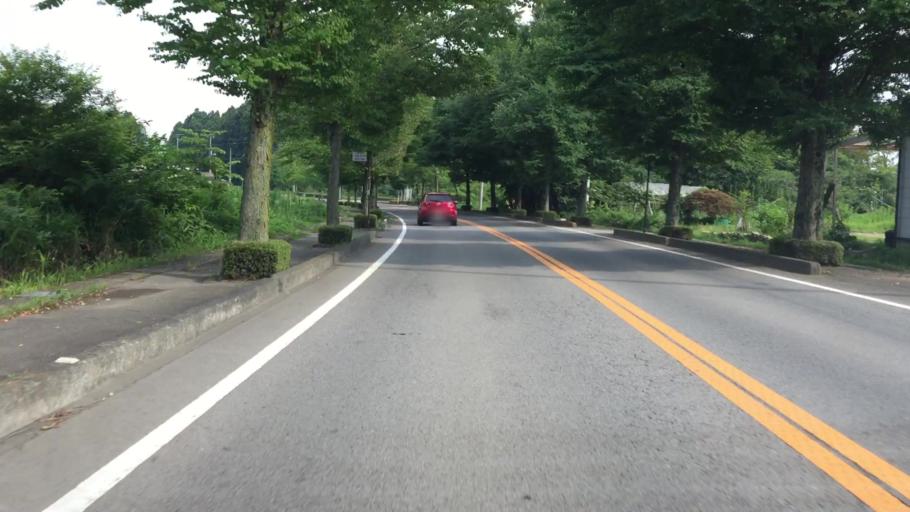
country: JP
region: Tochigi
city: Kuroiso
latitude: 36.9730
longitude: 139.9712
